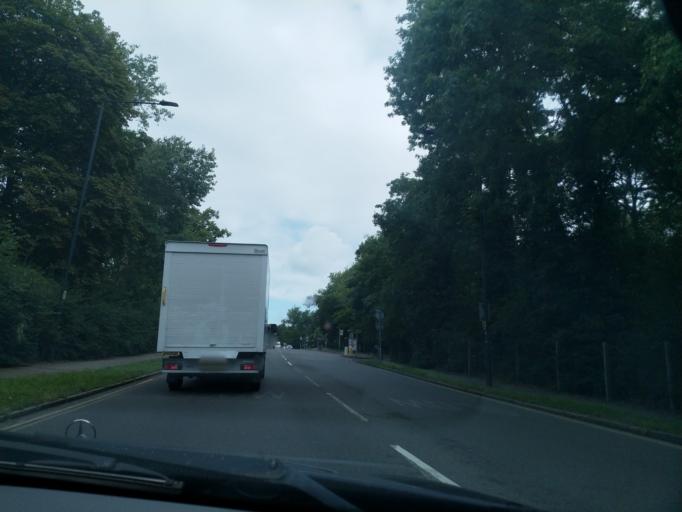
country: GB
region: England
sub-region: Greater London
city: Harrow
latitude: 51.5742
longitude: -0.3250
